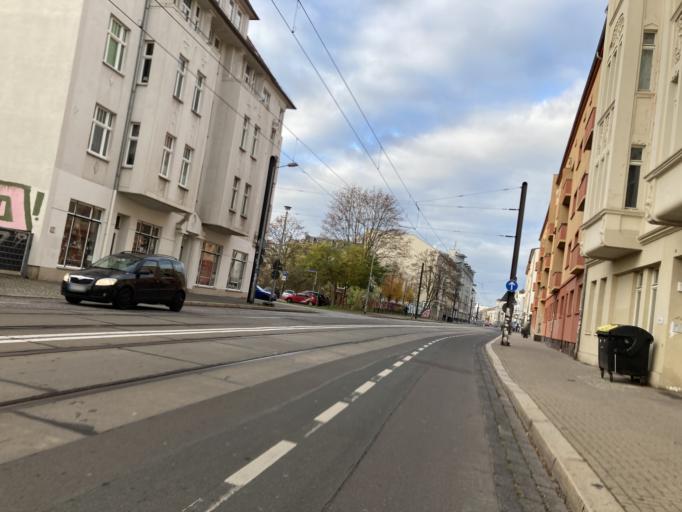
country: DE
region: Saxony-Anhalt
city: Magdeburg
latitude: 52.1304
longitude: 11.6156
